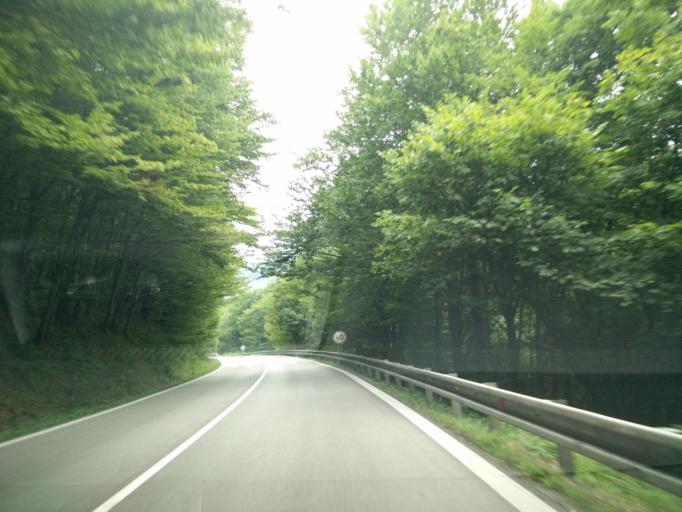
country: SK
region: Nitriansky
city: Handlova
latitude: 48.6589
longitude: 18.7337
